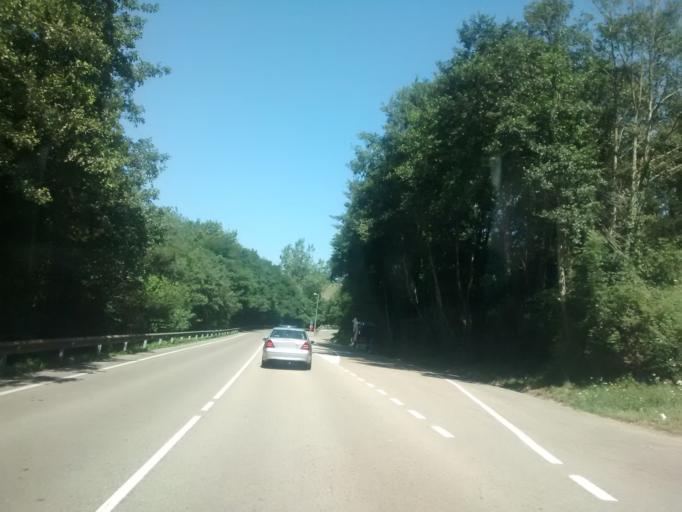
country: ES
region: Cantabria
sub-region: Provincia de Cantabria
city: San Miguel de Meruelo
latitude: 43.4359
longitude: -3.5690
